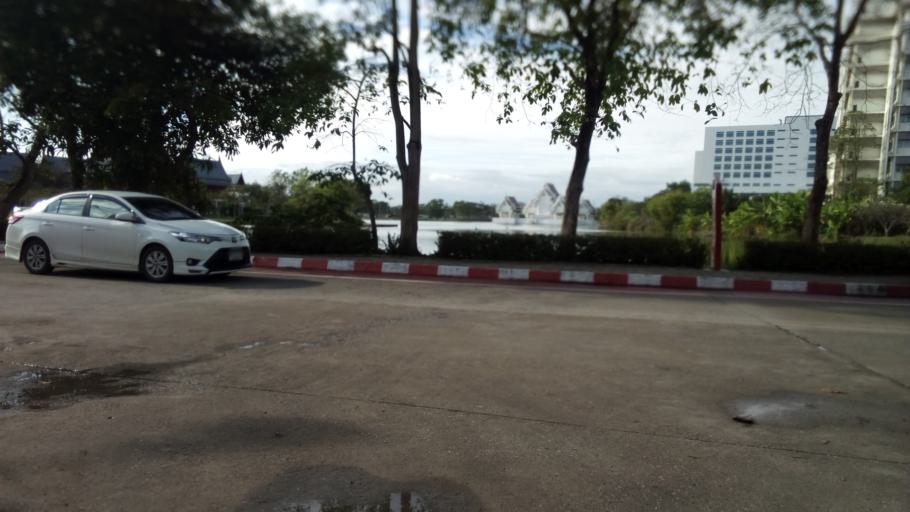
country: TH
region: Nakhon Nayok
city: Ongkharak
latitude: 14.1082
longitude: 100.9850
